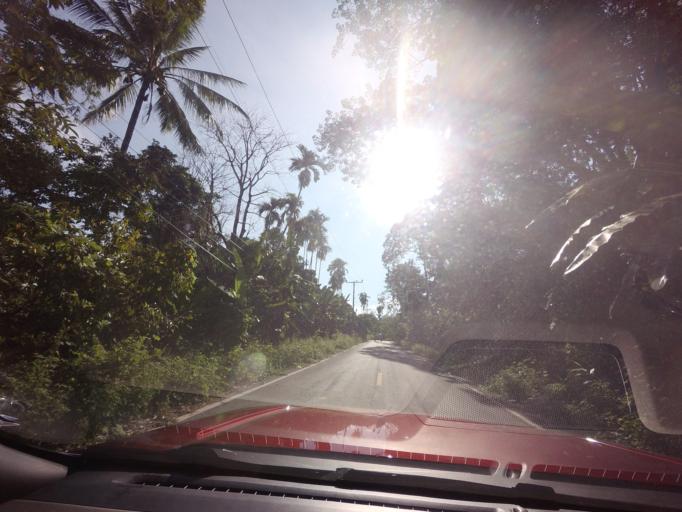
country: TH
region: Yala
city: Than To
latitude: 6.0709
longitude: 101.3484
